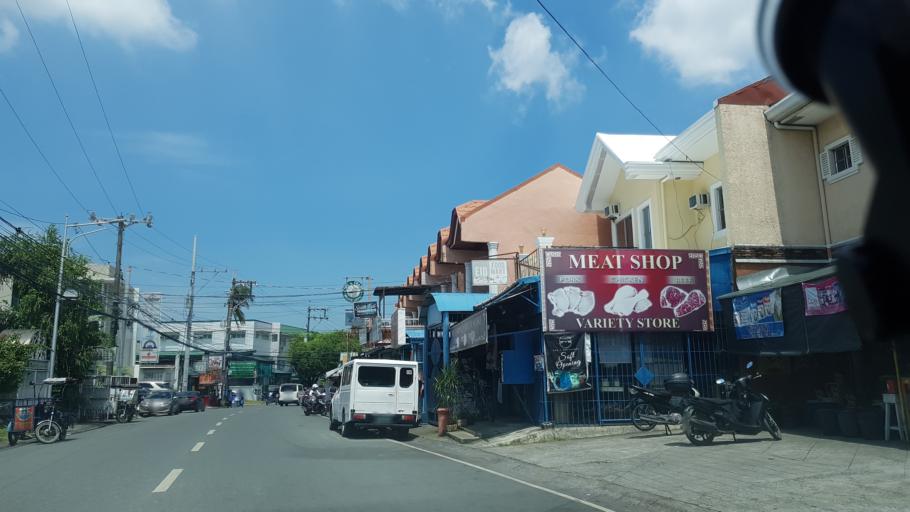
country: PH
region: Calabarzon
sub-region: Province of Rizal
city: Las Pinas
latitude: 14.4407
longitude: 120.9844
